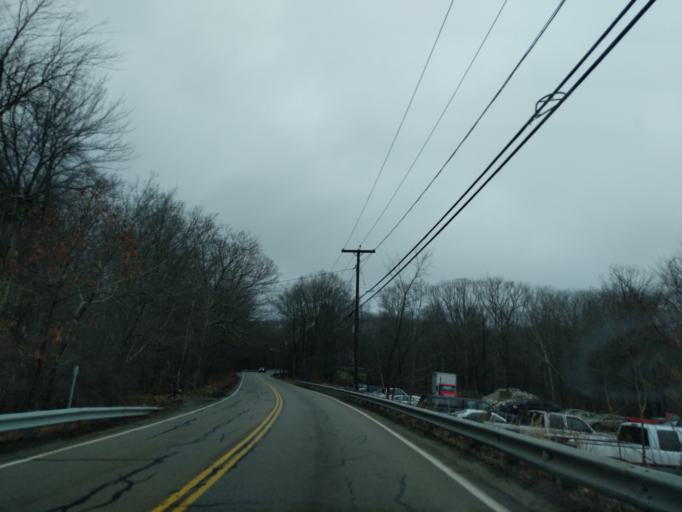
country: US
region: Massachusetts
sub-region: Worcester County
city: Webster
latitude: 42.0551
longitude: -71.8319
